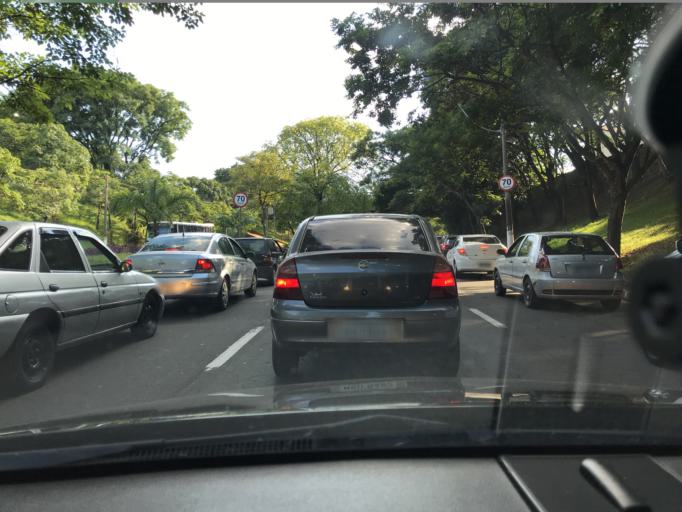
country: BR
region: Sao Paulo
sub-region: Campinas
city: Campinas
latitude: -22.9147
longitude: -47.0593
